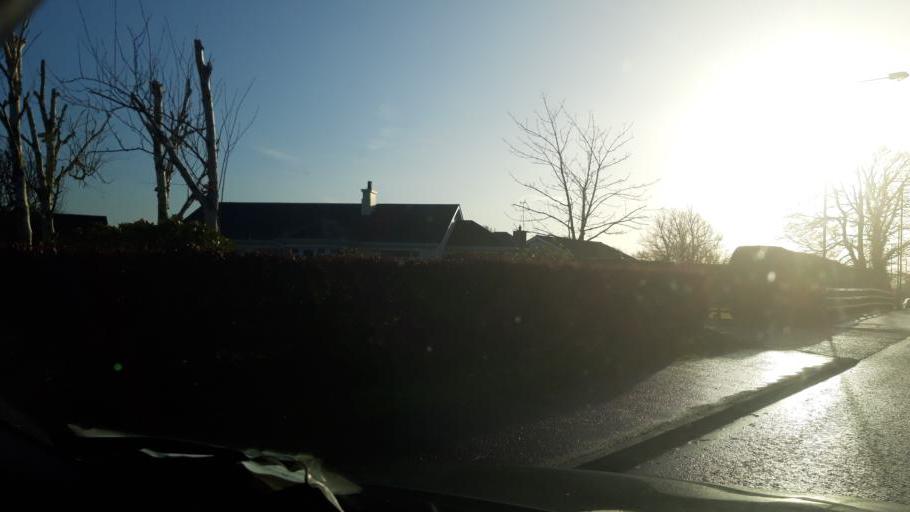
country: GB
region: Northern Ireland
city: Garvagh
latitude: 54.9901
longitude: -6.6845
